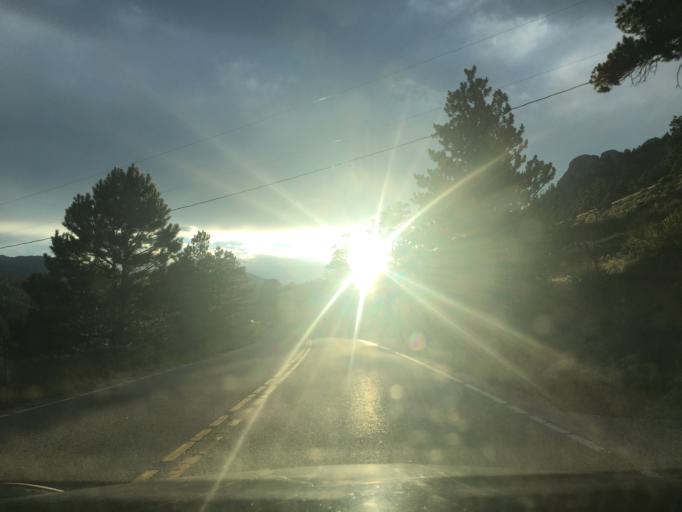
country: US
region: Colorado
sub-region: Larimer County
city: Estes Park
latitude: 40.3991
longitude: -105.5706
